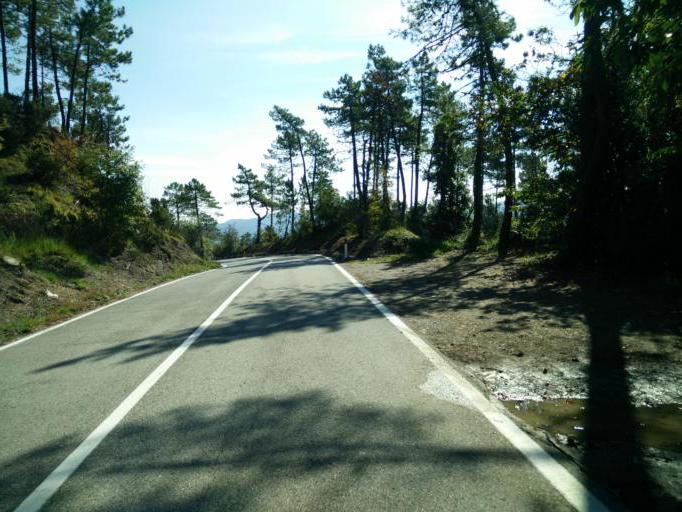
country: IT
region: Liguria
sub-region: Provincia di La Spezia
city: Framura
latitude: 44.2476
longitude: 9.5880
